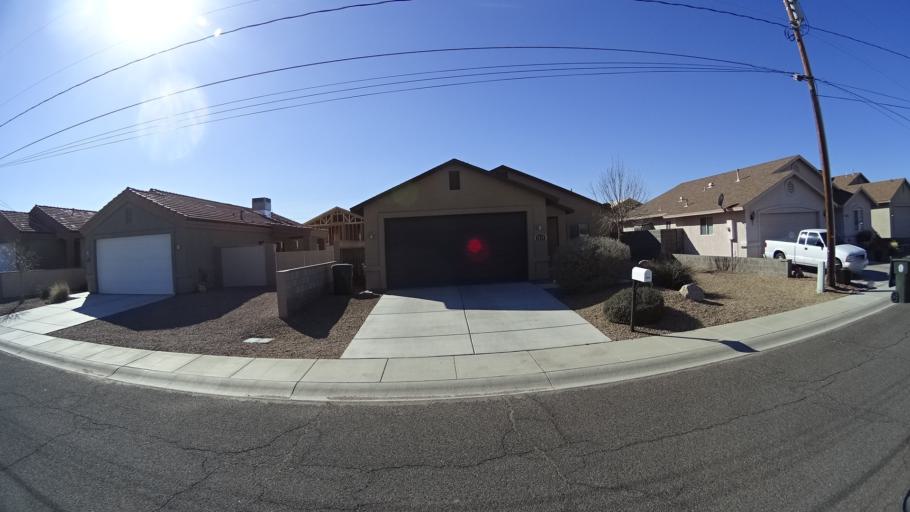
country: US
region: Arizona
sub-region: Mohave County
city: Kingman
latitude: 35.1986
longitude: -114.0171
